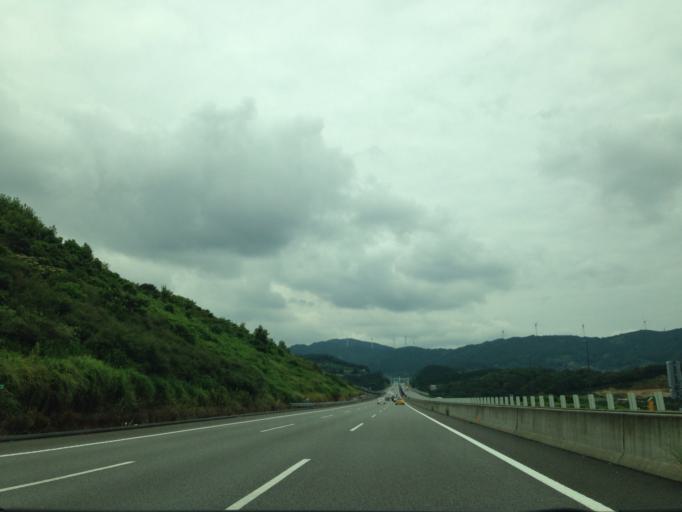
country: JP
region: Shizuoka
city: Hamakita
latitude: 34.8426
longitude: 137.7475
